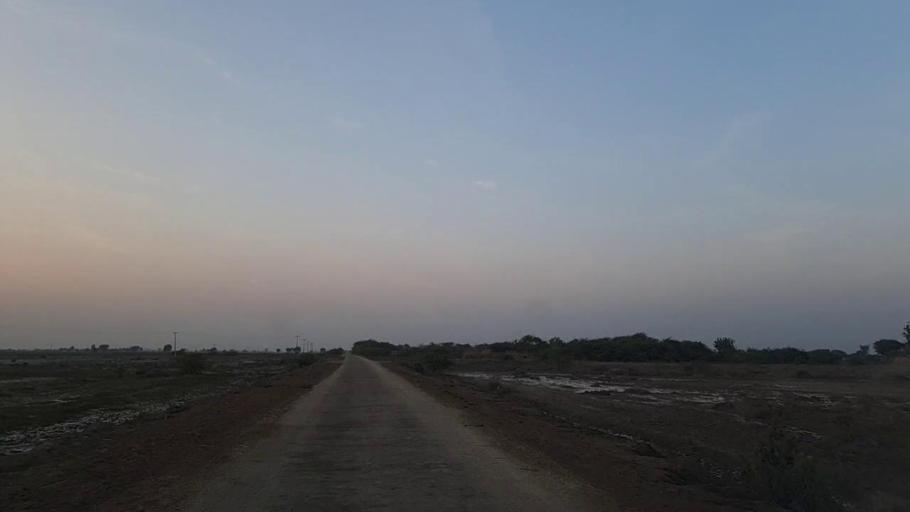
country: PK
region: Sindh
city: Naukot
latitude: 24.9755
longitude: 69.4315
